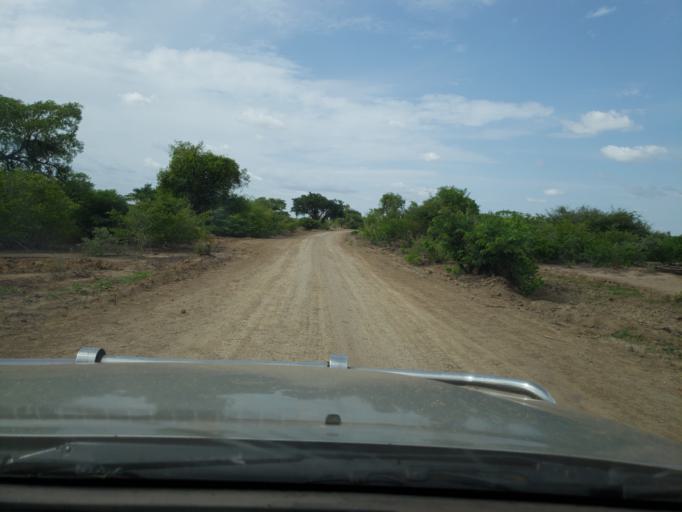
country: ML
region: Segou
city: Bla
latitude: 12.7581
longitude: -5.6267
